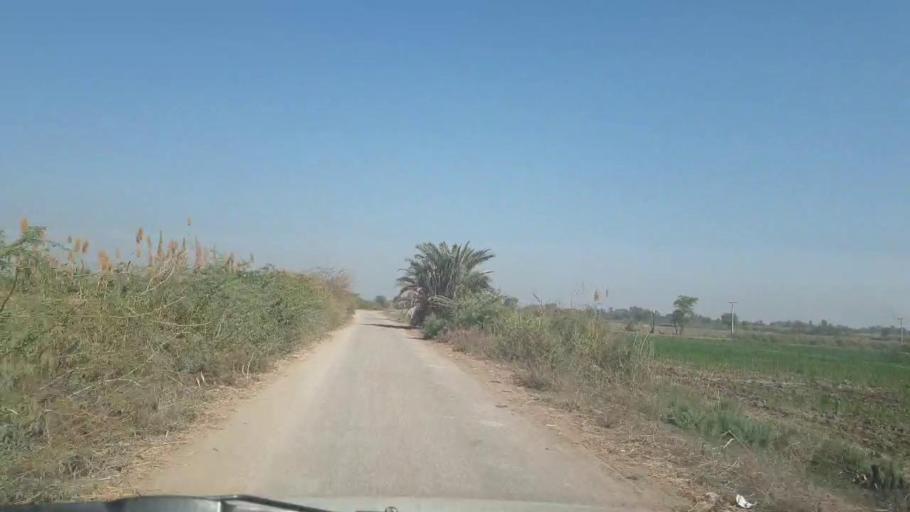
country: PK
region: Sindh
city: Mirpur Khas
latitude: 25.5102
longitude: 69.1715
